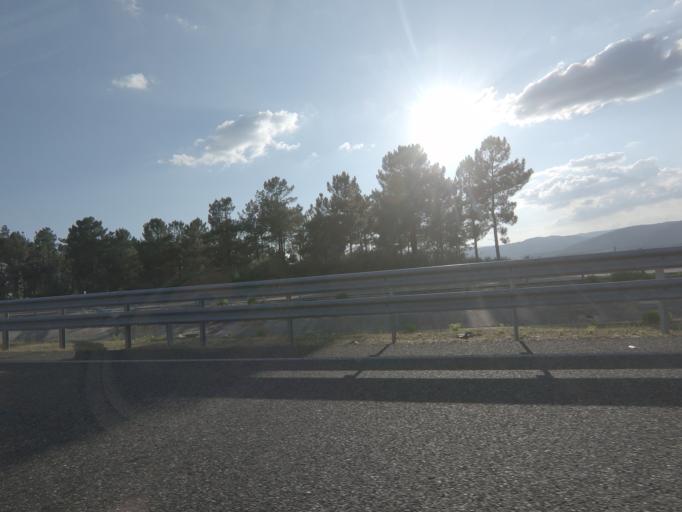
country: ES
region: Galicia
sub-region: Provincia de Ourense
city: Oimbra
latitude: 41.8932
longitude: -7.4243
